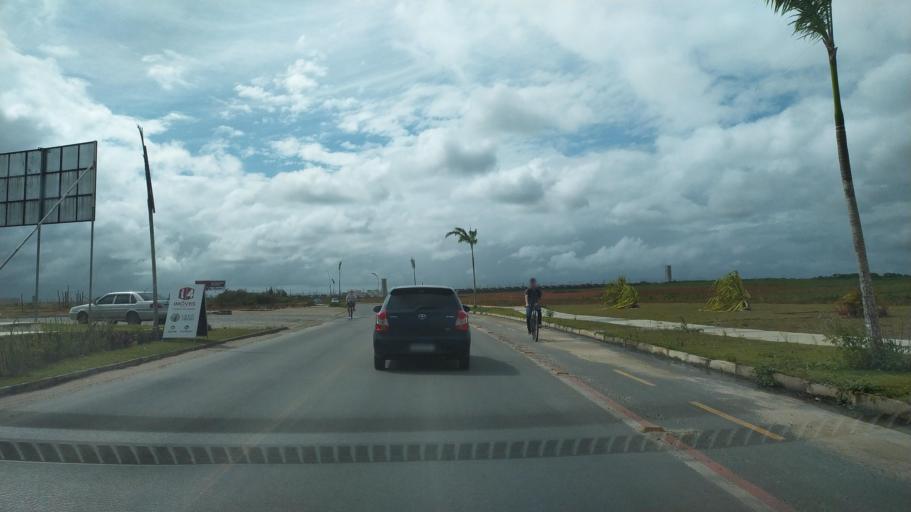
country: BR
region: Alagoas
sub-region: Satuba
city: Satuba
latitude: -9.5359
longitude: -35.7663
